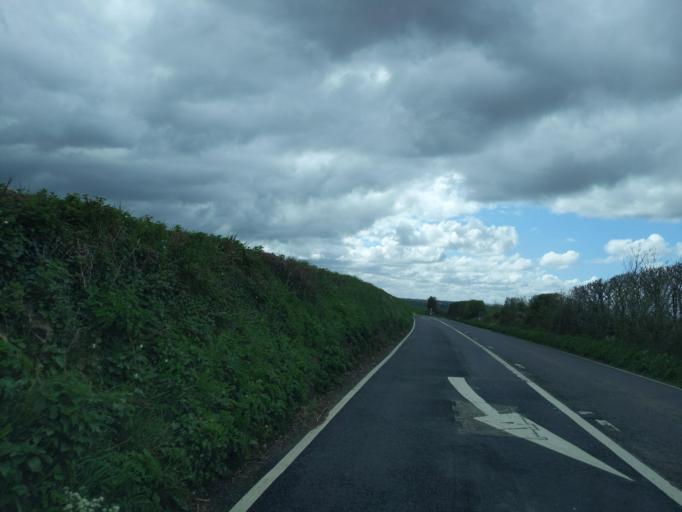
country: GB
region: England
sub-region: Cornwall
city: Pensilva
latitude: 50.4776
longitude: -4.3910
